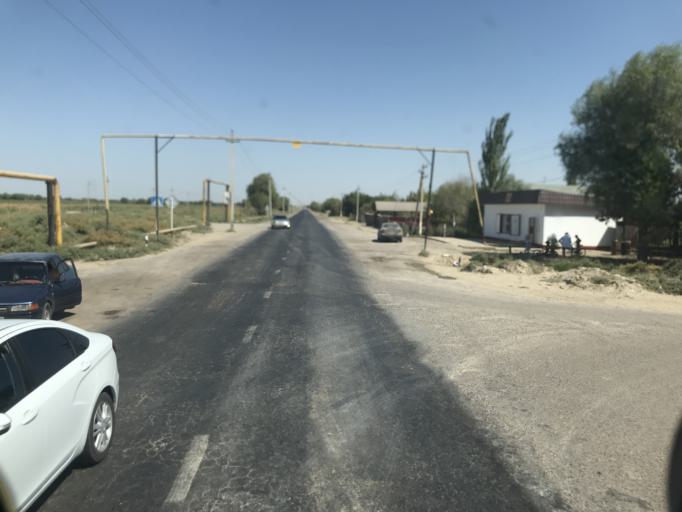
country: KZ
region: Ongtustik Qazaqstan
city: Ilyich
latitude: 40.8964
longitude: 68.4881
